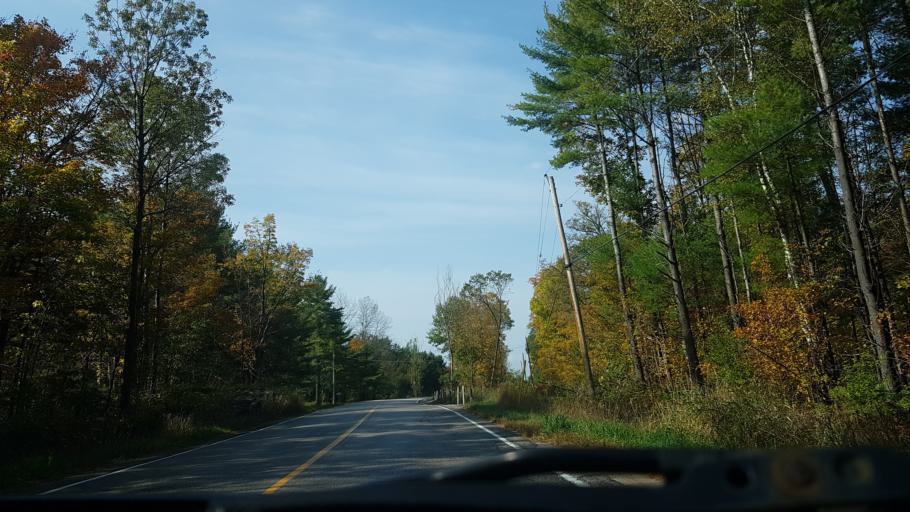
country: CA
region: Ontario
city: Gravenhurst
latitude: 44.7809
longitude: -79.2701
